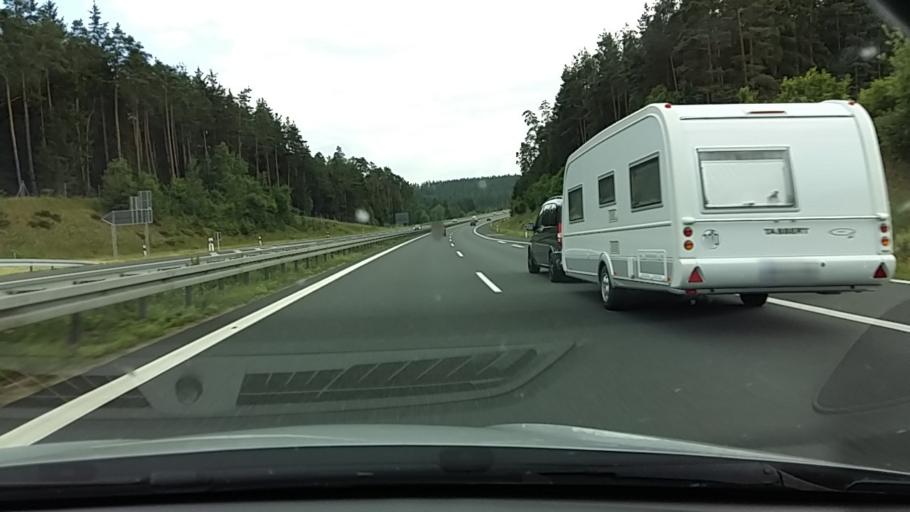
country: DE
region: Bavaria
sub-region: Upper Palatinate
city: Wernberg-Koblitz
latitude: 49.5388
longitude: 12.1925
